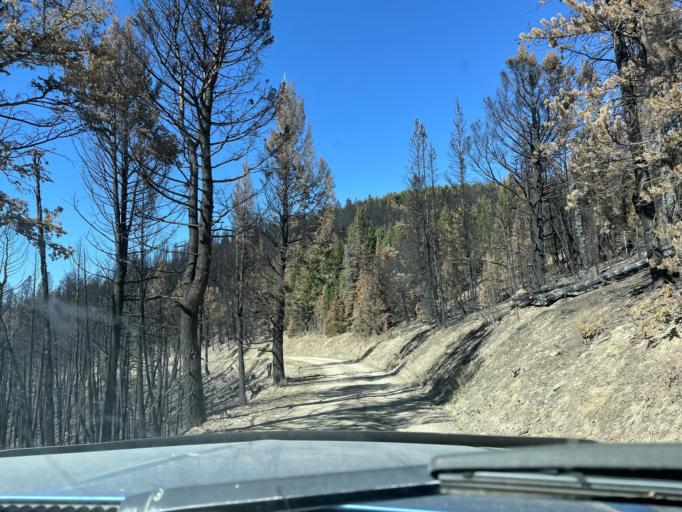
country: US
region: Montana
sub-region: Broadwater County
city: Townsend
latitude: 46.5064
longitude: -111.2758
